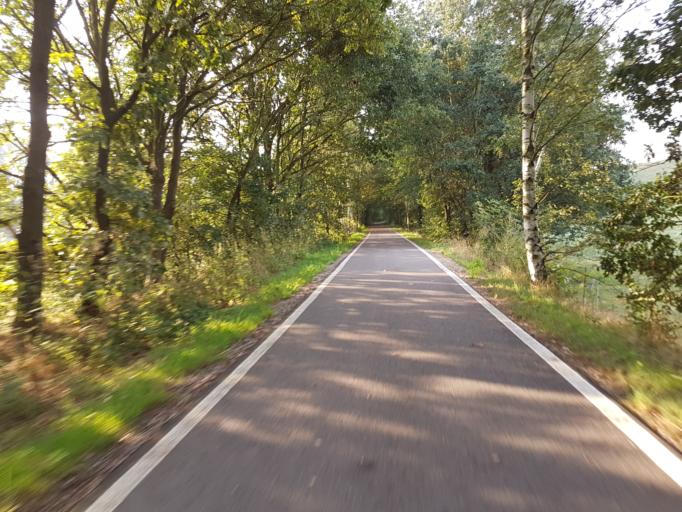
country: DE
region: Saxony
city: Wittgensdorf
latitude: 50.8885
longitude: 12.8905
